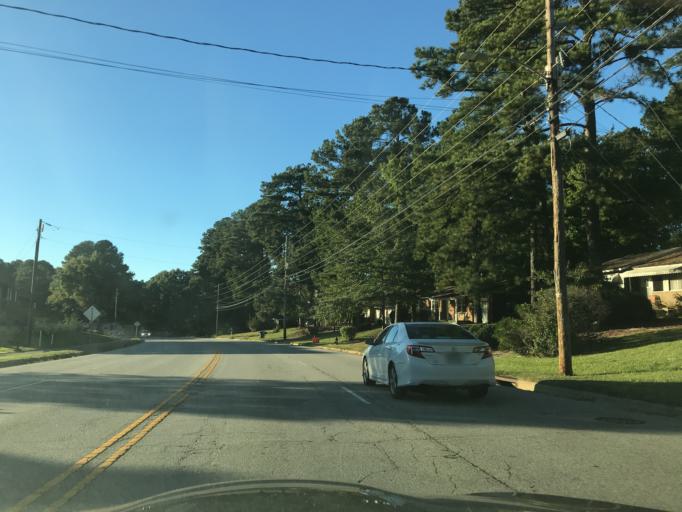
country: US
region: North Carolina
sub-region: Wake County
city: Raleigh
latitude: 35.7492
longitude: -78.6078
